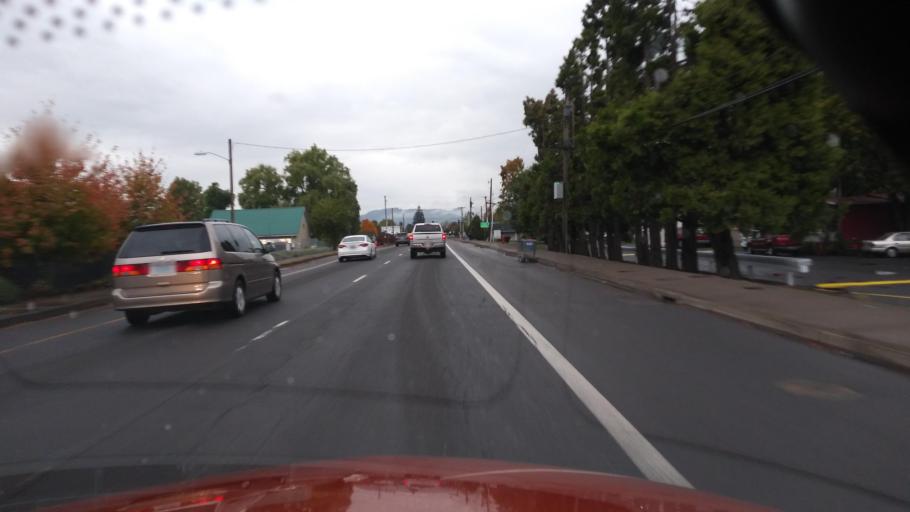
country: US
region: Oregon
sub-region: Washington County
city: Cornelius
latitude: 45.5210
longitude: -123.0636
